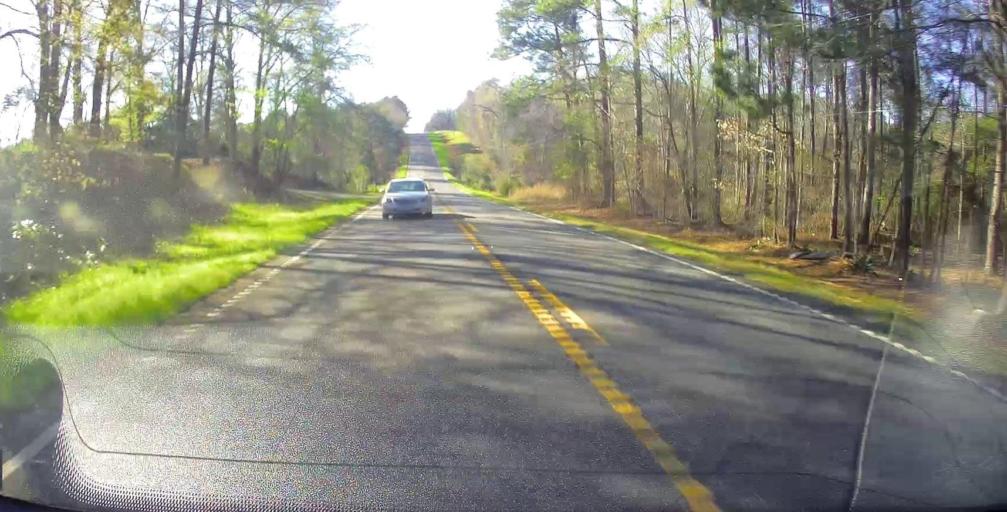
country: US
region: Georgia
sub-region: Macon County
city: Marshallville
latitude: 32.4428
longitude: -83.8937
